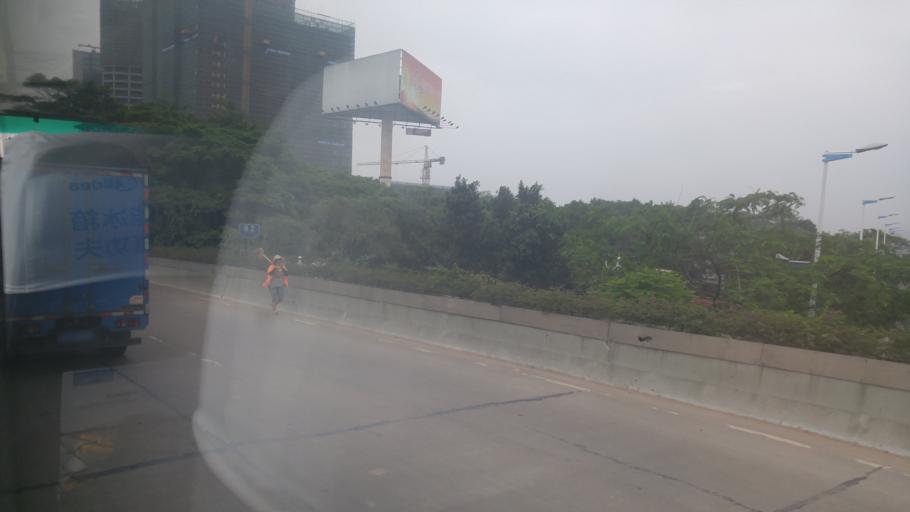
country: CN
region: Guangdong
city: Dali
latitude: 23.1089
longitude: 113.1365
